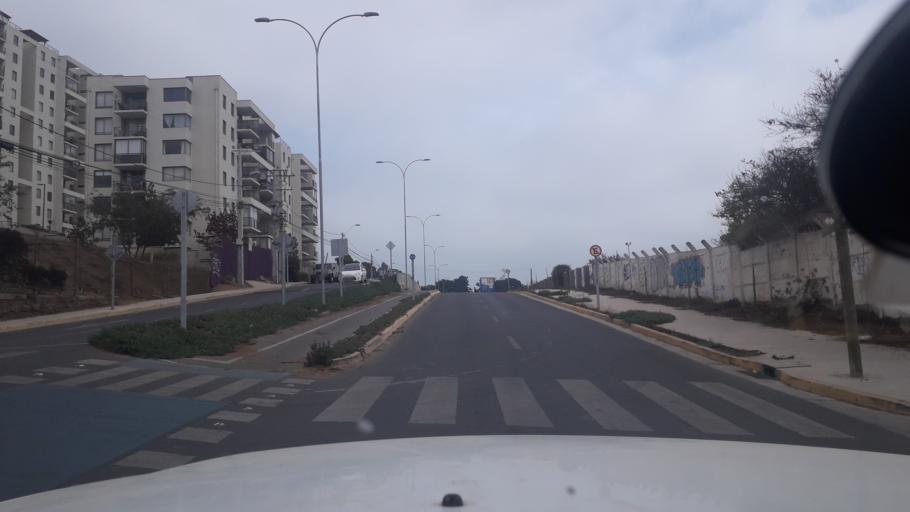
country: CL
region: Valparaiso
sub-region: Provincia de Valparaiso
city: Vina del Mar
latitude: -32.9370
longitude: -71.5334
